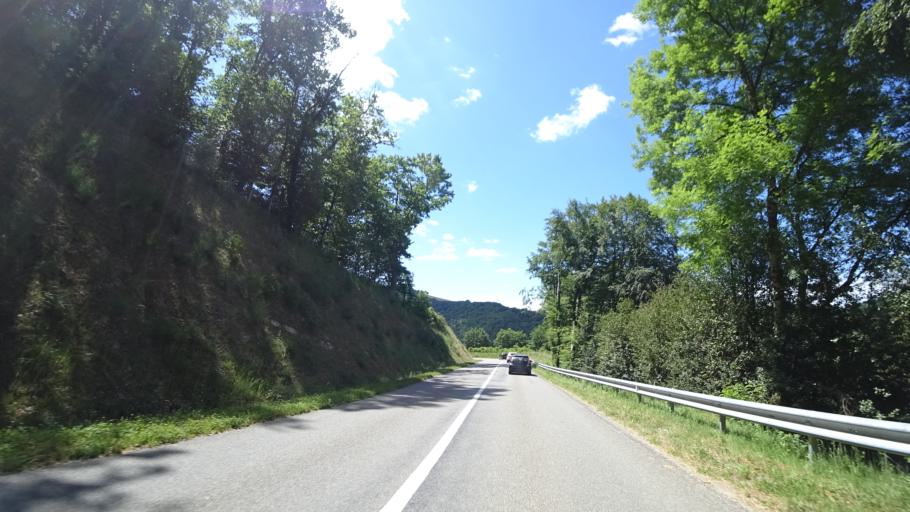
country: FR
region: Midi-Pyrenees
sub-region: Departement de l'Aveyron
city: Colombies
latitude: 44.3835
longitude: 2.3039
